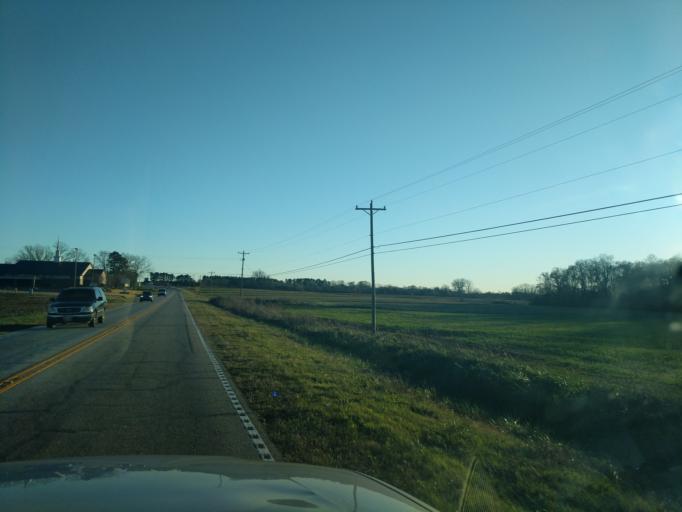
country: US
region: Georgia
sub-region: Hart County
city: Reed Creek
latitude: 34.5340
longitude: -82.8464
